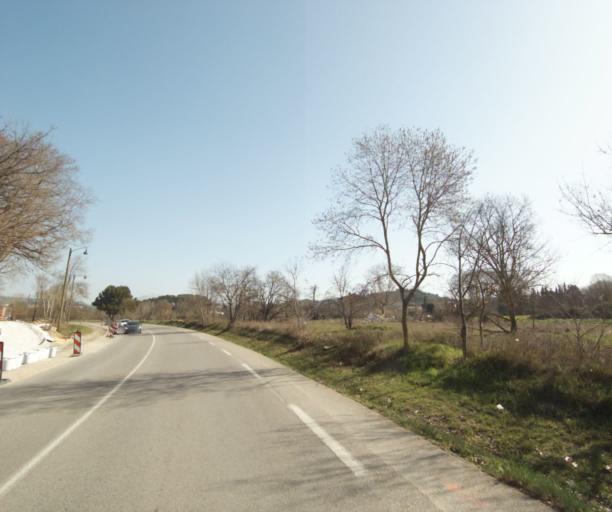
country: FR
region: Provence-Alpes-Cote d'Azur
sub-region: Departement des Bouches-du-Rhone
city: Aix-en-Provence
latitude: 43.5078
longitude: 5.4277
